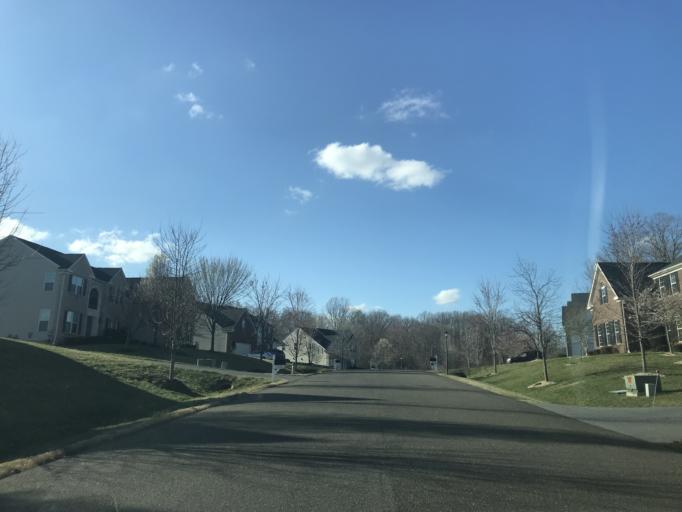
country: US
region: Maryland
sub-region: Prince George's County
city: Woodmore
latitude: 38.9105
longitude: -76.7927
